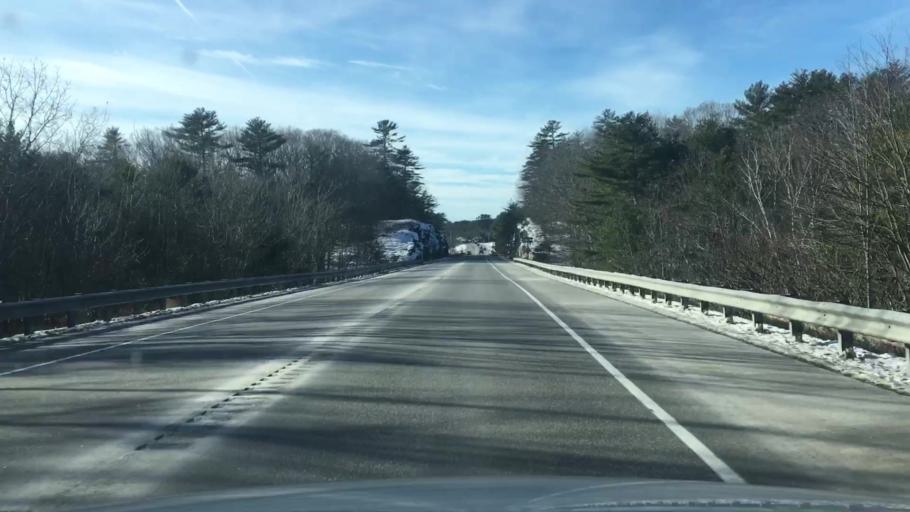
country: US
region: Maine
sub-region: Sagadahoc County
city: Woolwich
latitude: 43.9371
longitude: -69.7729
